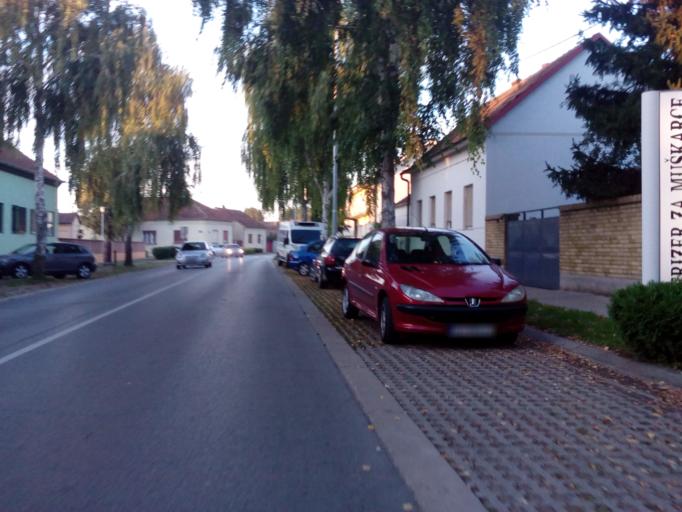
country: HR
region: Vukovarsko-Srijemska
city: Vinkovci
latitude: 45.2925
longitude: 18.8115
